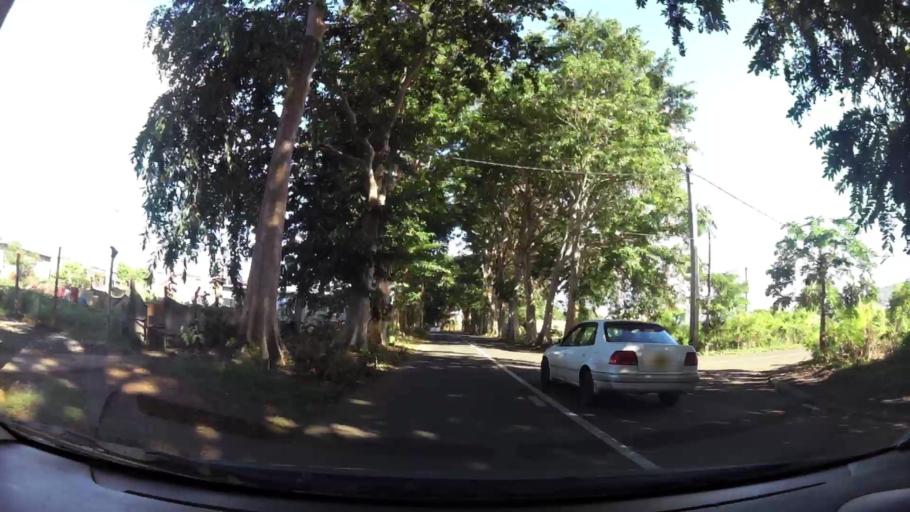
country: MU
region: Grand Port
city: Mahebourg
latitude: -20.4091
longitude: 57.6946
